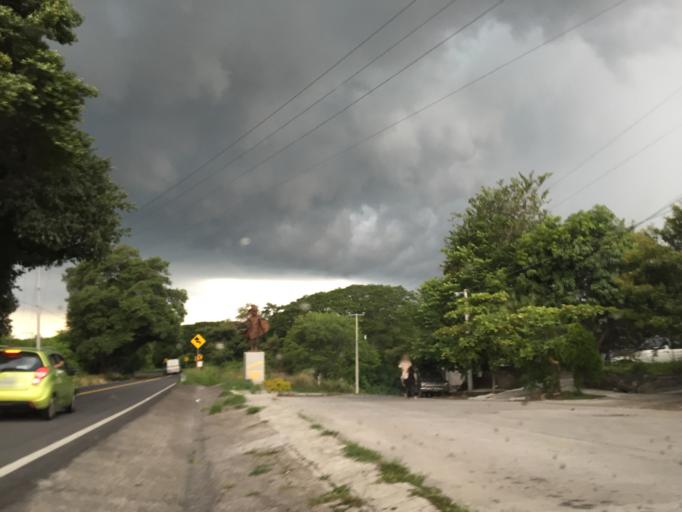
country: MX
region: Colima
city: Cuauhtemoc
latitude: 19.3335
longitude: -103.5911
